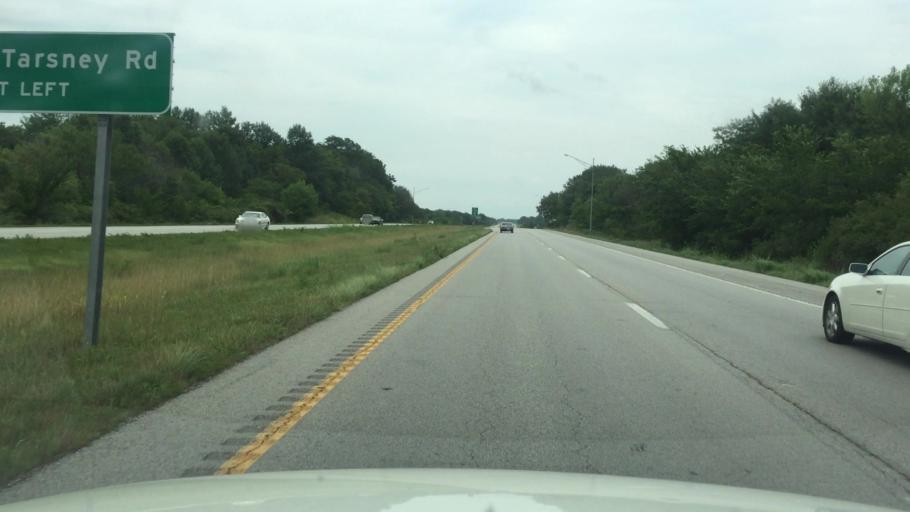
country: US
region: Missouri
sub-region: Jackson County
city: Lake Lotawana
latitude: 38.8827
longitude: -94.2231
